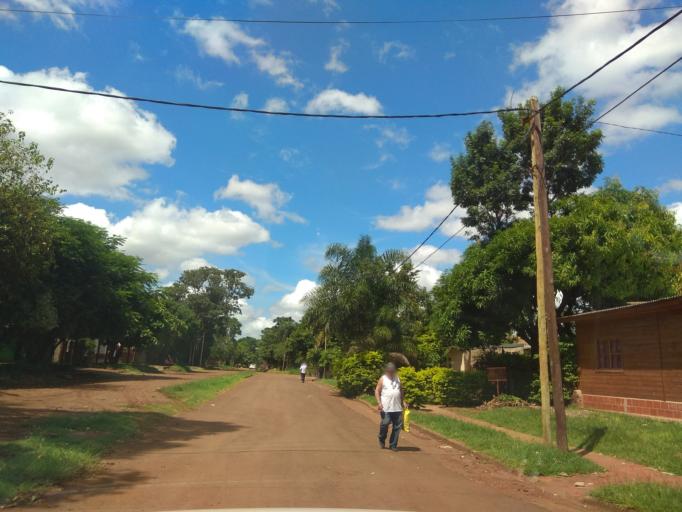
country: AR
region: Misiones
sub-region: Departamento de Capital
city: Posadas
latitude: -27.3860
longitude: -55.9230
